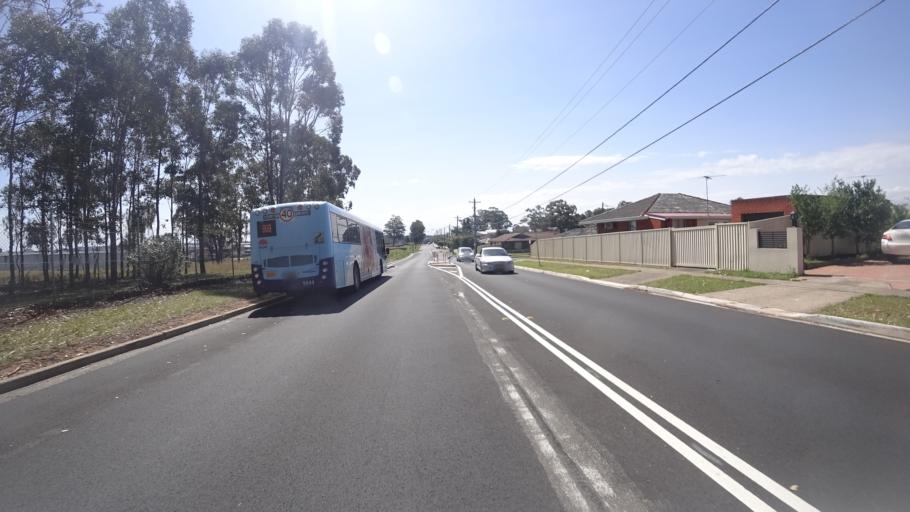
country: AU
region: New South Wales
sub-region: Liverpool
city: Miller
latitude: -33.9408
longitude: 150.8890
